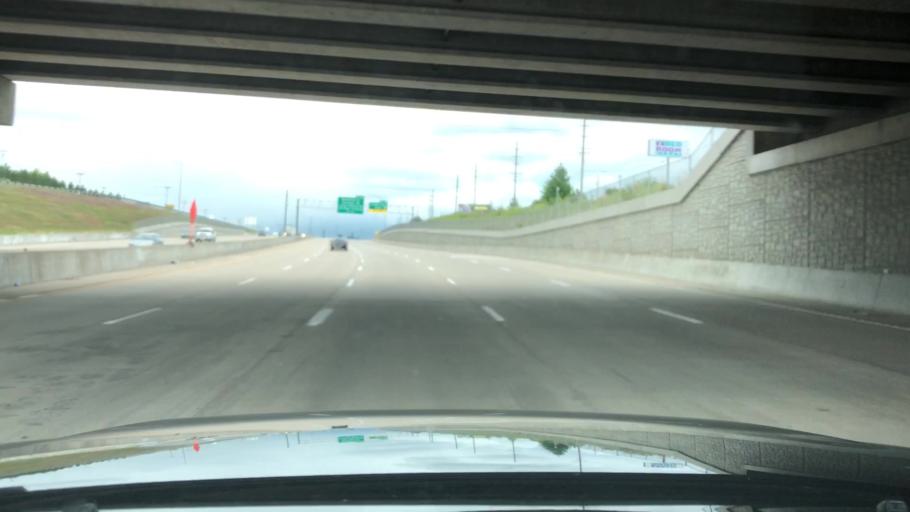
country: US
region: Missouri
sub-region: Saint Charles County
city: Cottleville
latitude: 38.7416
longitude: -90.6091
